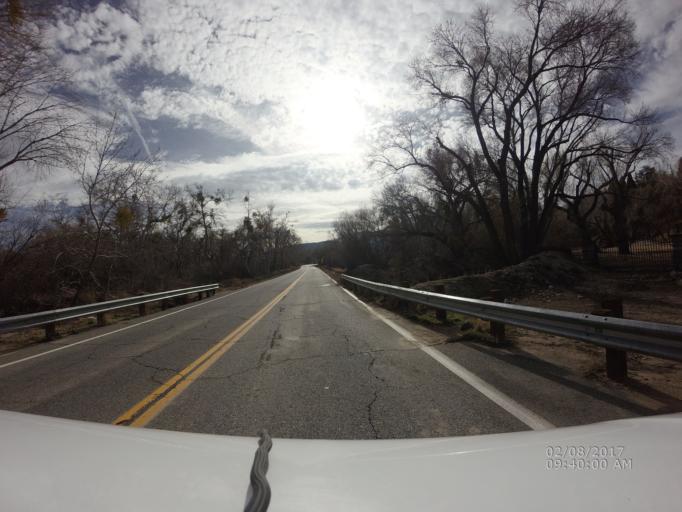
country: US
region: California
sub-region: Los Angeles County
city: Littlerock
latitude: 34.4521
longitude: -117.8562
